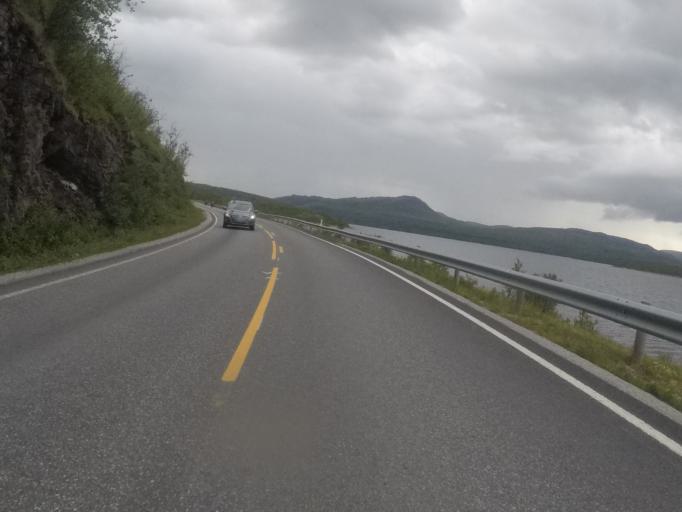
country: NO
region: Finnmark Fylke
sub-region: Porsanger
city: Lakselv
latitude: 69.9173
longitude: 24.9803
